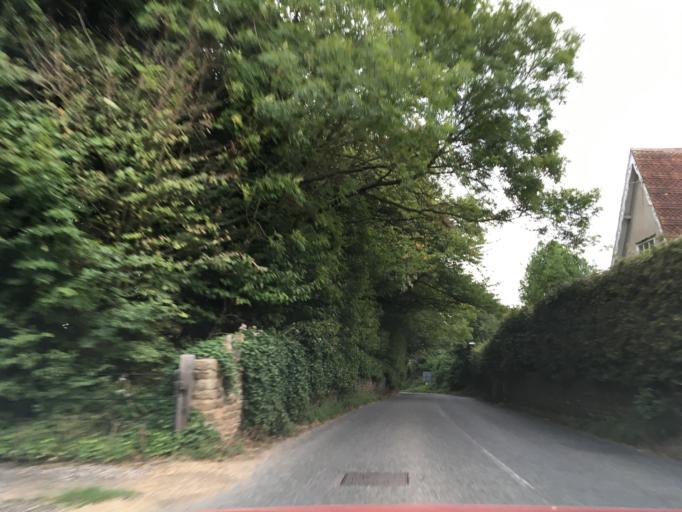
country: GB
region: England
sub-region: Wiltshire
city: Bremhill
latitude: 51.4343
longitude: -2.0643
